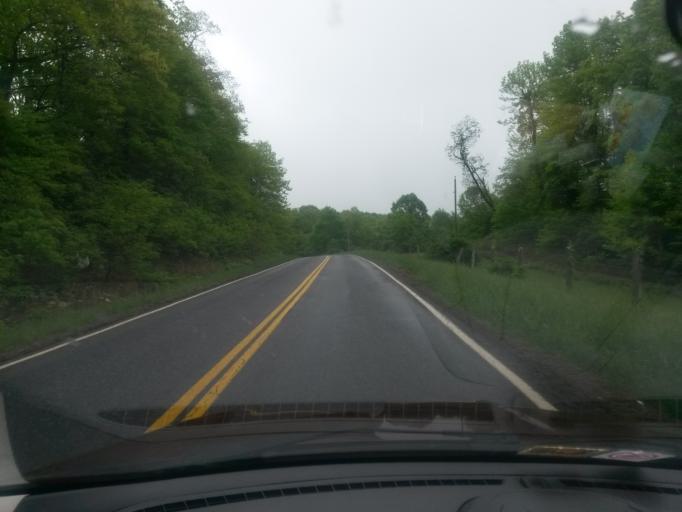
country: US
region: Virginia
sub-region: Floyd County
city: Floyd
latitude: 36.7737
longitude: -80.3898
